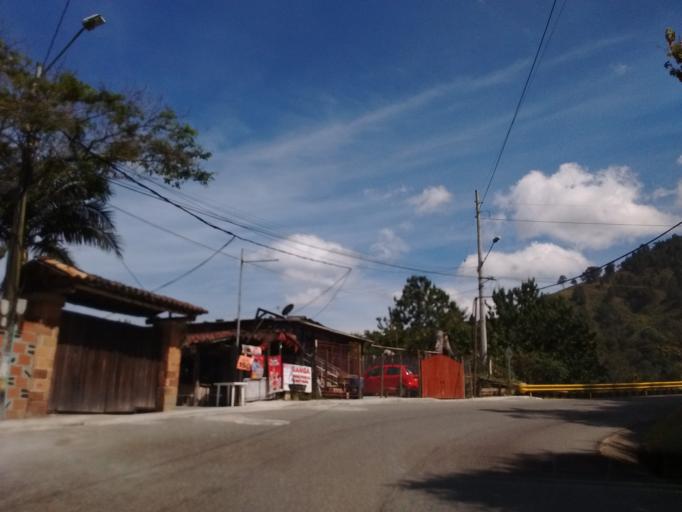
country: CO
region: Antioquia
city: Medellin
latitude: 6.2387
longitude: -75.5180
